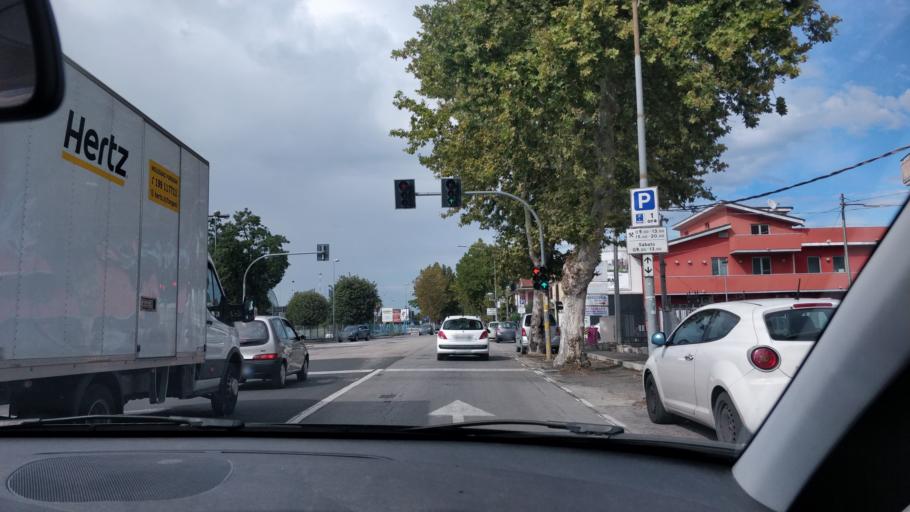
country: IT
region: Abruzzo
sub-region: Provincia di Chieti
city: Sambuceto
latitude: 42.4281
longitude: 14.1876
